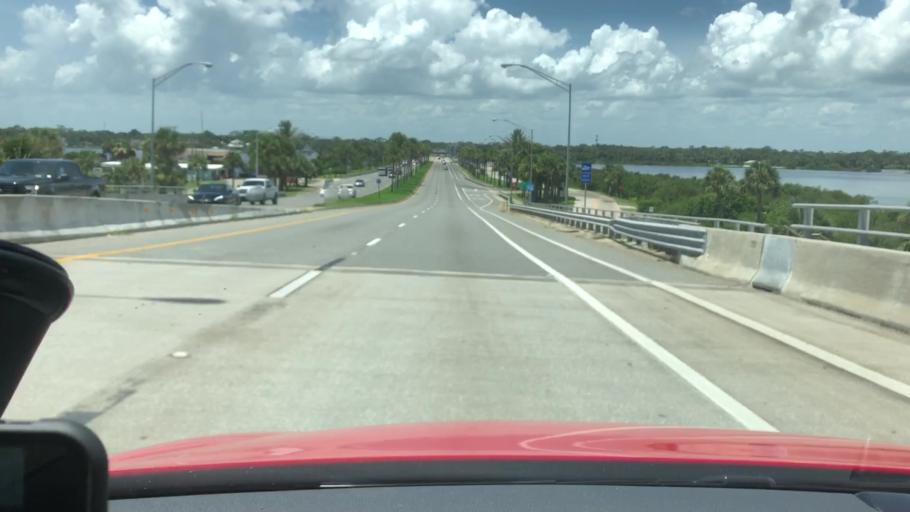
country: US
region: Florida
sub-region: Volusia County
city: Port Orange
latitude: 29.1484
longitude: -80.9774
